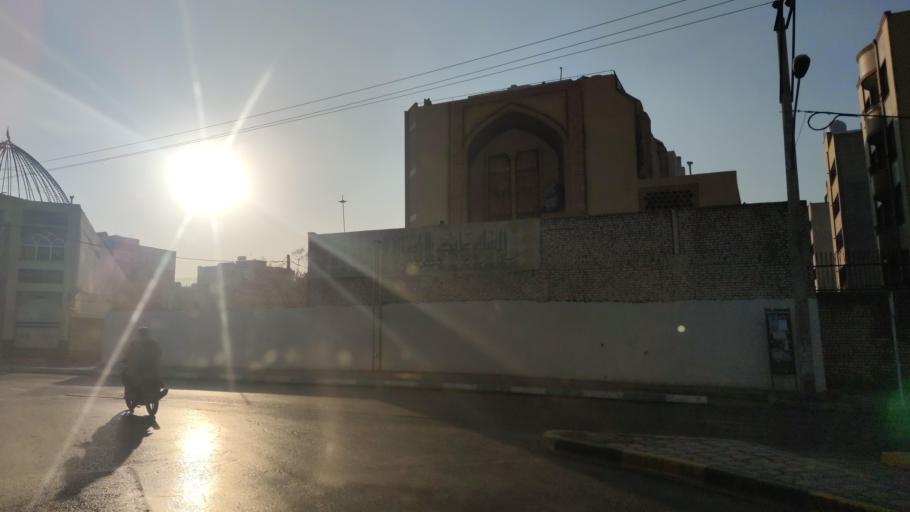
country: IR
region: Isfahan
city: Isfahan
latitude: 32.7082
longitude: 51.6804
